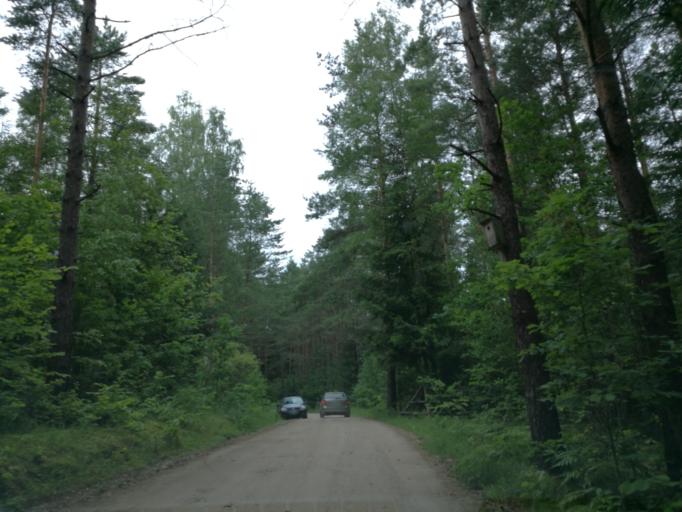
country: LT
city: Trakai
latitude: 54.6483
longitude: 24.9643
